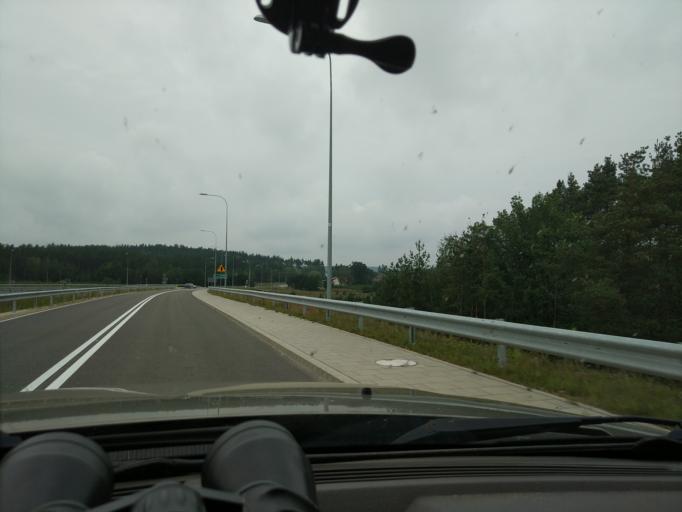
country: PL
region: Podlasie
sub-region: Powiat zambrowski
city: Szumowo
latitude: 52.9114
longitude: 22.0969
